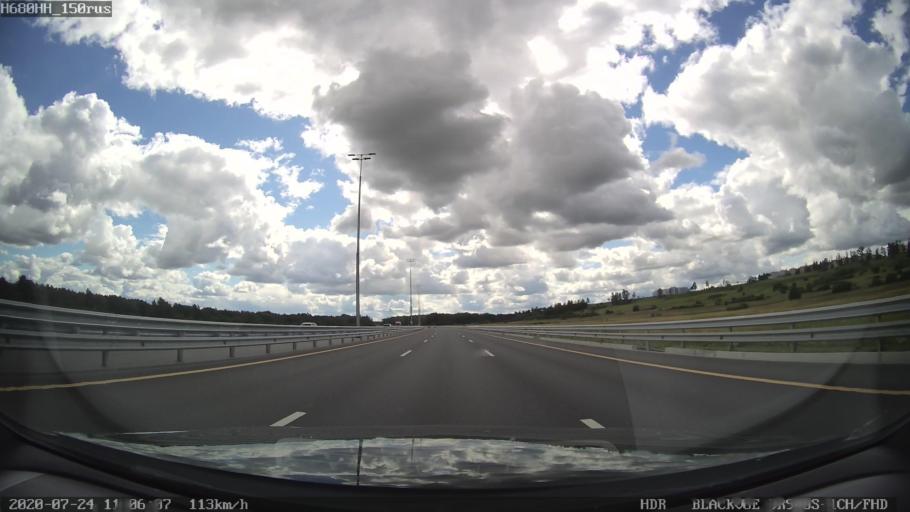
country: RU
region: St.-Petersburg
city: Shushary
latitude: 59.7677
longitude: 30.3675
